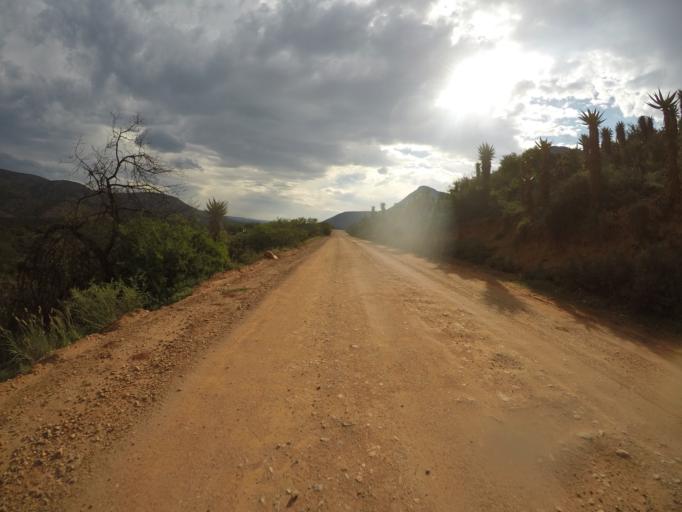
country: ZA
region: Eastern Cape
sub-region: Cacadu District Municipality
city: Kareedouw
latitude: -33.5823
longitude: 24.1600
